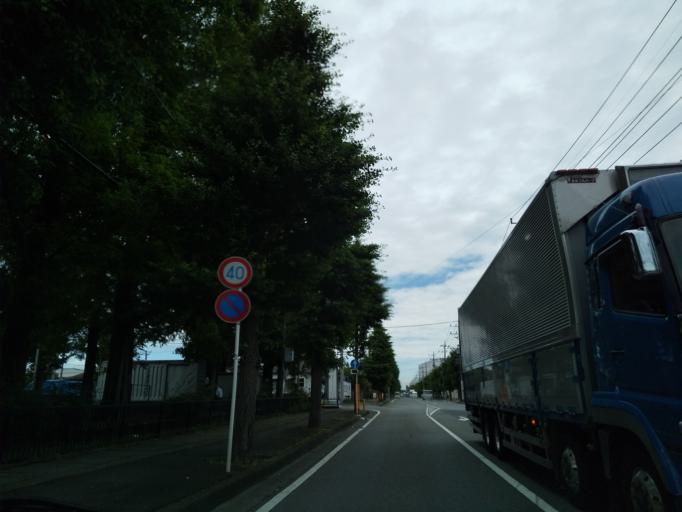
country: JP
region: Kanagawa
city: Zama
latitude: 35.5108
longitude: 139.3579
